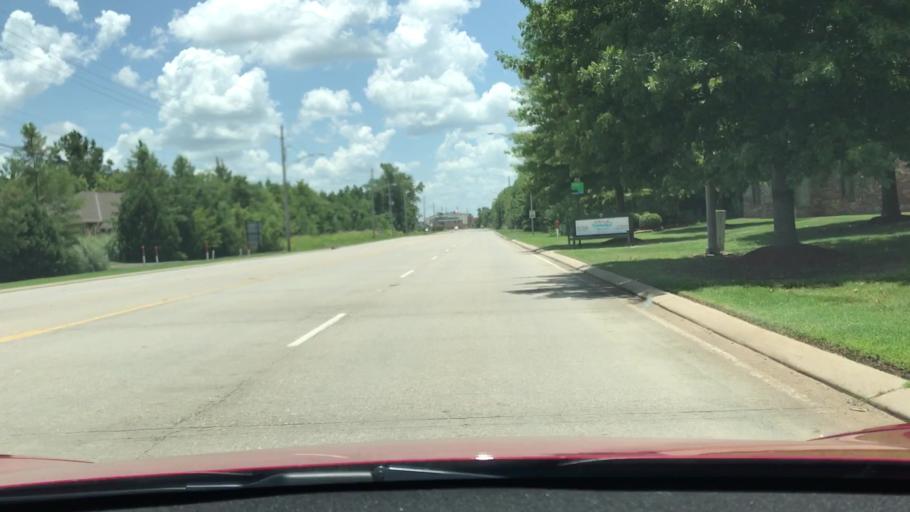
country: US
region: Louisiana
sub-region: Bossier Parish
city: Bossier City
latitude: 32.4315
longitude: -93.7260
